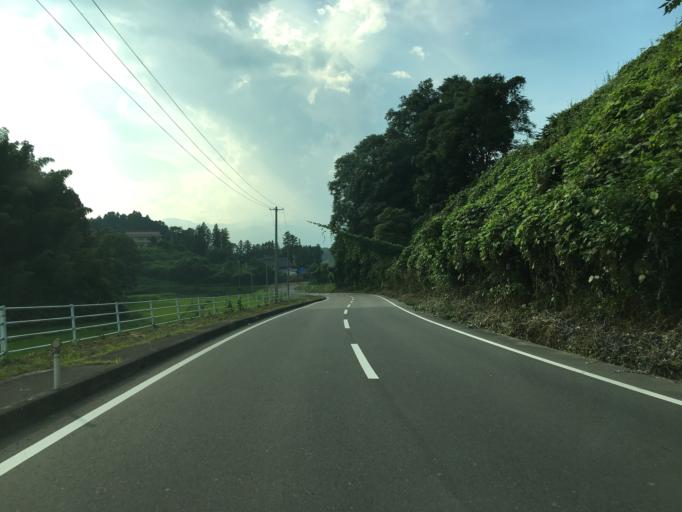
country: JP
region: Fukushima
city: Nihommatsu
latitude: 37.5505
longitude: 140.4395
